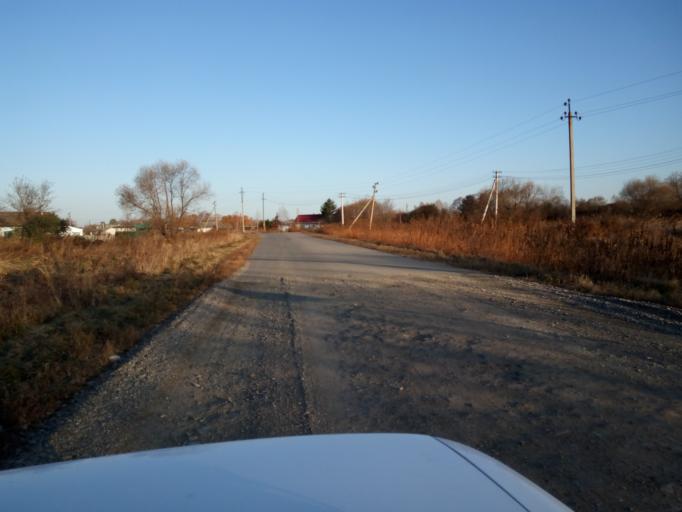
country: RU
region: Primorskiy
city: Lazo
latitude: 45.8571
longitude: 133.6461
